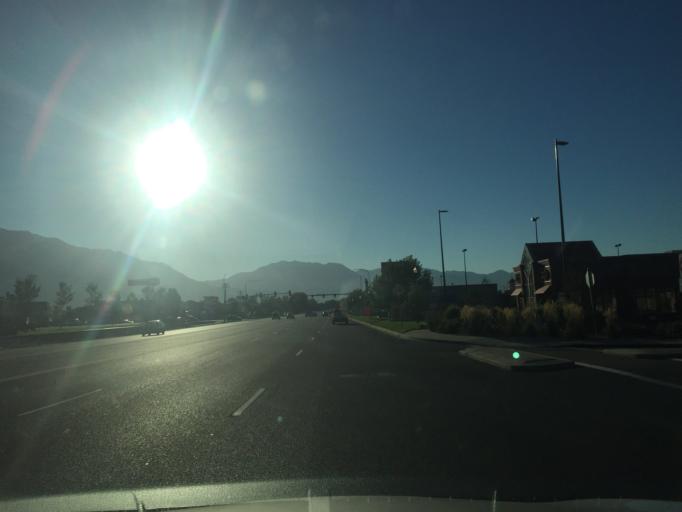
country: US
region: Utah
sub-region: Utah County
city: Lehi
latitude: 40.3876
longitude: -111.8239
